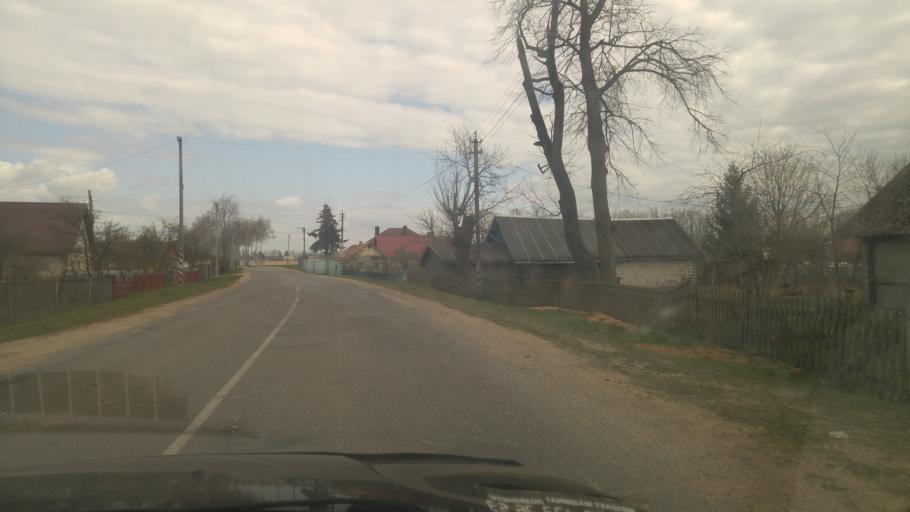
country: BY
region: Minsk
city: Rudzyensk
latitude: 53.6584
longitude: 27.7870
